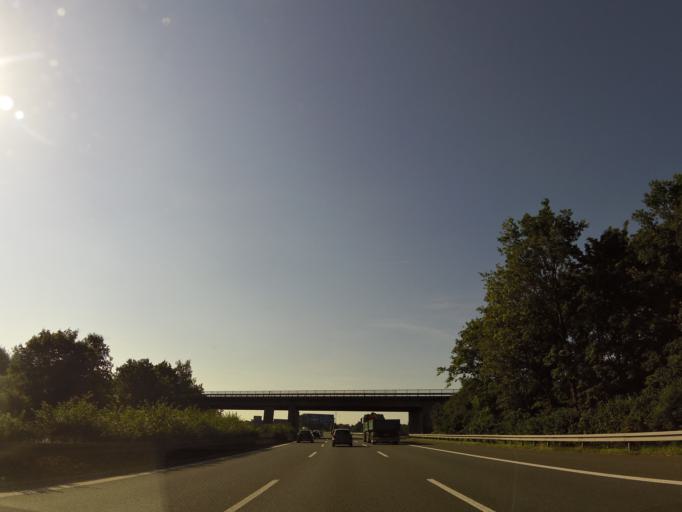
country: DE
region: Bavaria
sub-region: Regierungsbezirk Mittelfranken
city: Erlangen
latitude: 49.5451
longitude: 11.0163
